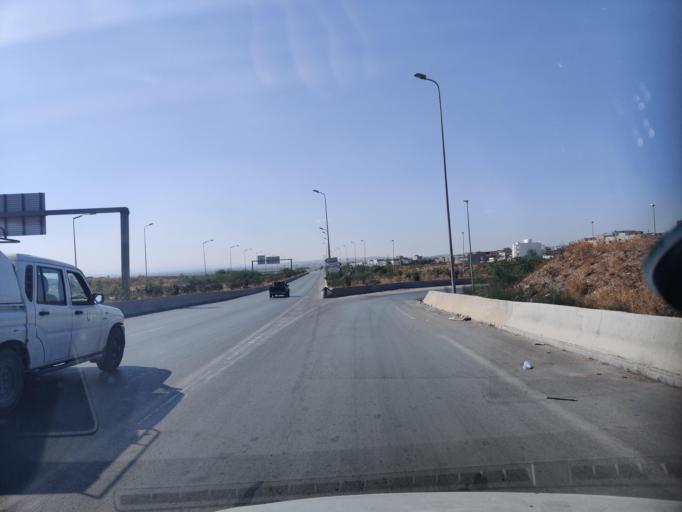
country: TN
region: Manouba
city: Manouba
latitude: 36.7799
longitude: 10.1191
